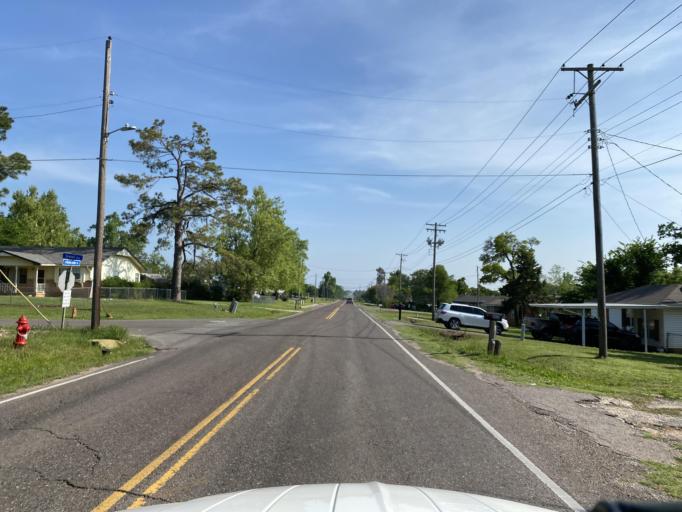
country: US
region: Oklahoma
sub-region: Oklahoma County
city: Nicoma Park
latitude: 35.4837
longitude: -97.3357
